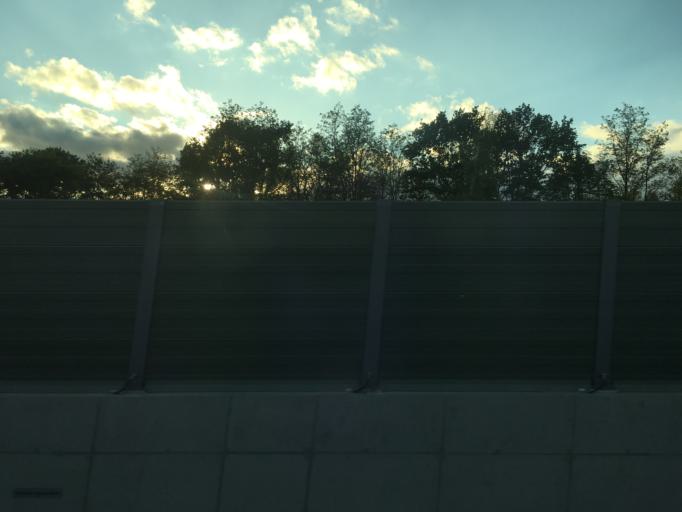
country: DE
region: Brandenburg
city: Elsterwerda
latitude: 51.4715
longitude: 13.5215
